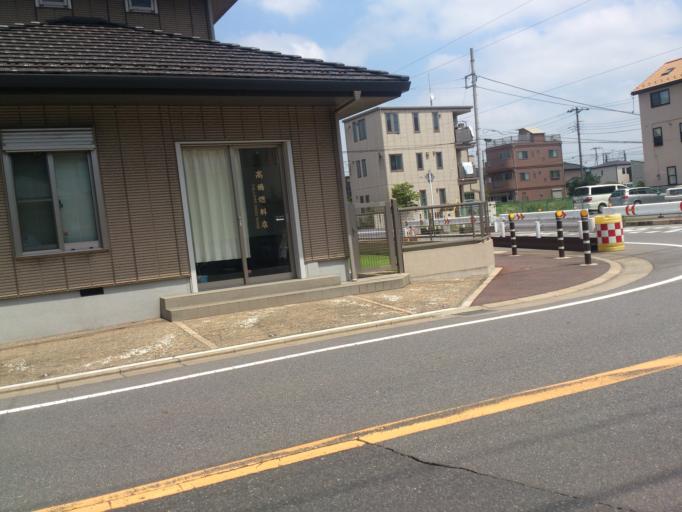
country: JP
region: Chiba
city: Chiba
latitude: 35.5995
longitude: 140.1195
